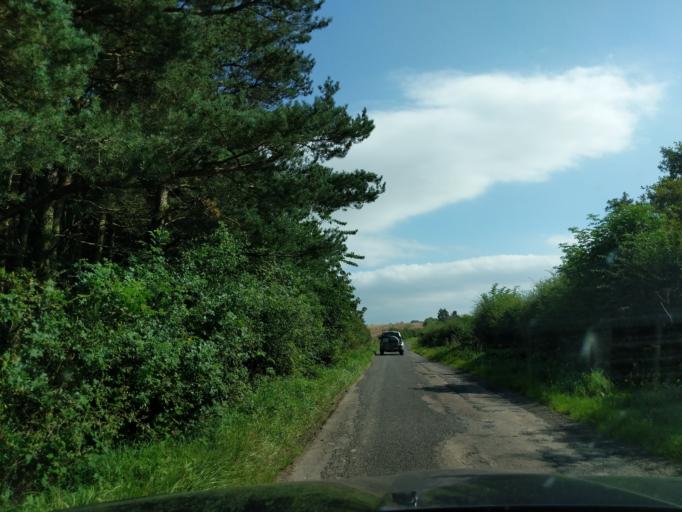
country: GB
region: England
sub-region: Northumberland
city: Ford
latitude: 55.6603
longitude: -2.1552
